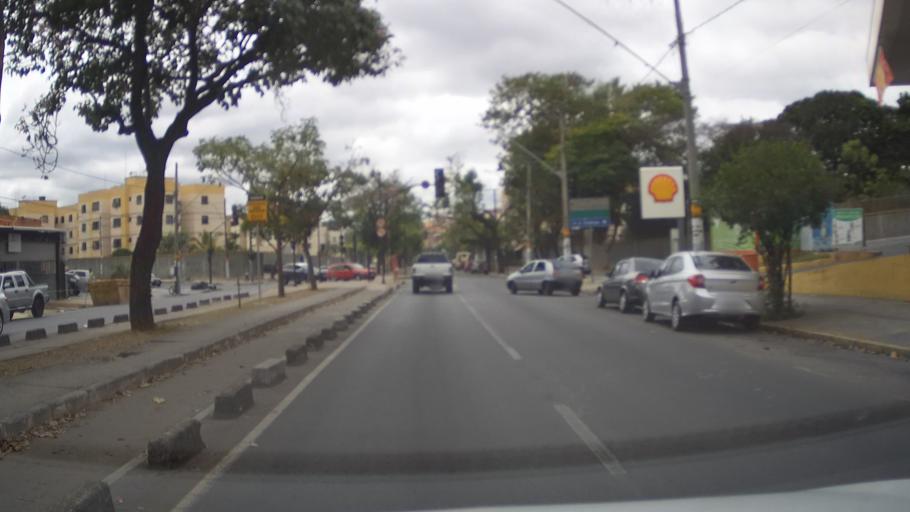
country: BR
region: Minas Gerais
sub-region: Belo Horizonte
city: Belo Horizonte
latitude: -19.8442
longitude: -43.9178
